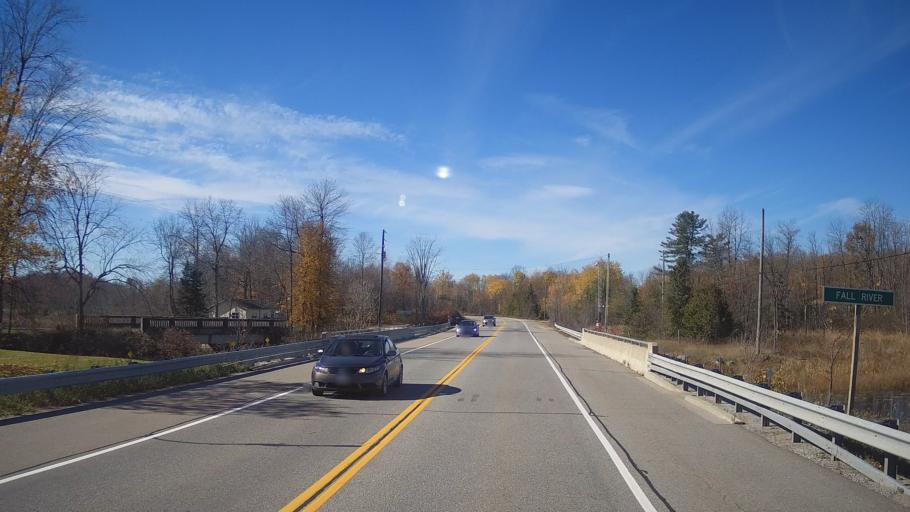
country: CA
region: Ontario
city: Perth
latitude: 44.8350
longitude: -76.5490
